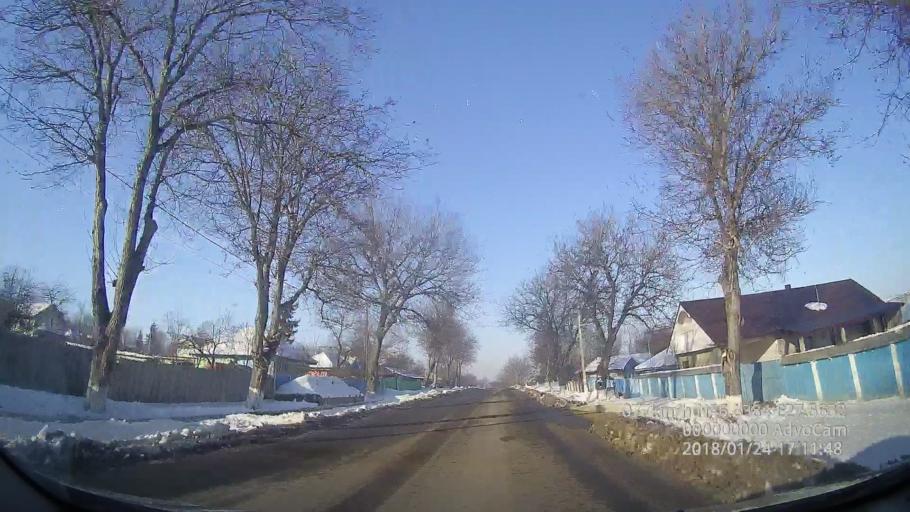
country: RO
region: Vaslui
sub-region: Comuna Rebricea
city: Rebricea
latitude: 46.8391
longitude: 27.5632
